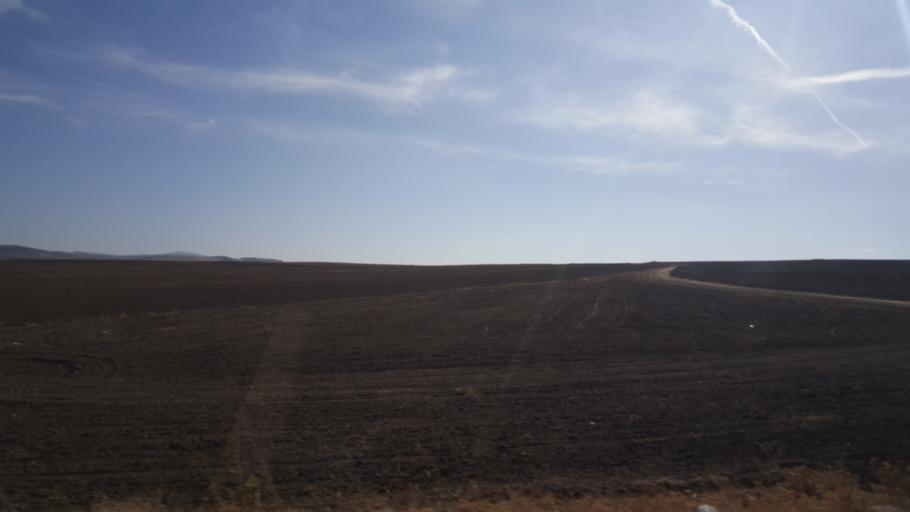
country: TR
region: Ankara
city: Yenice
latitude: 39.3804
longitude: 32.7725
